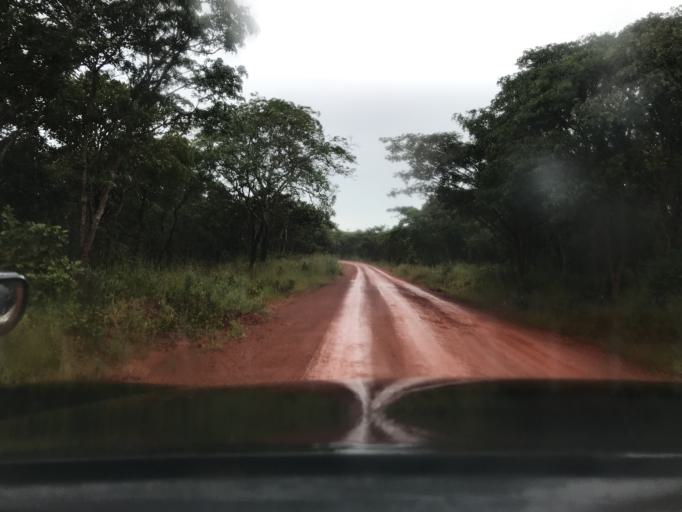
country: TZ
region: Kigoma
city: Uvinza
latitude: -5.2929
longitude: 30.3692
